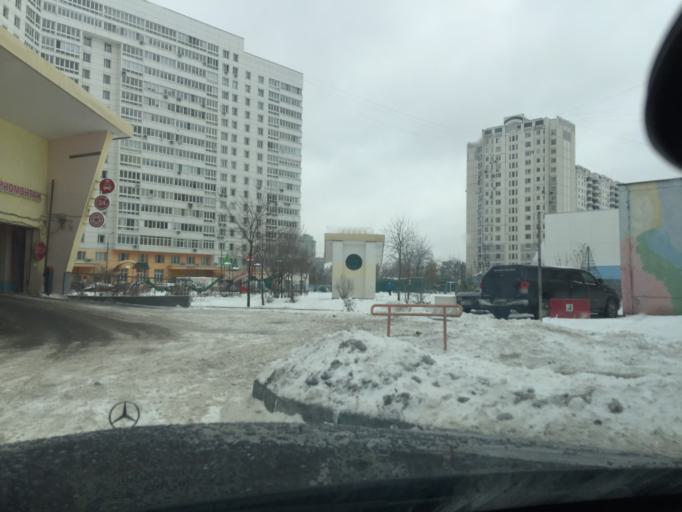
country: RU
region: Moscow
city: Troparevo
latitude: 55.6435
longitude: 37.4747
